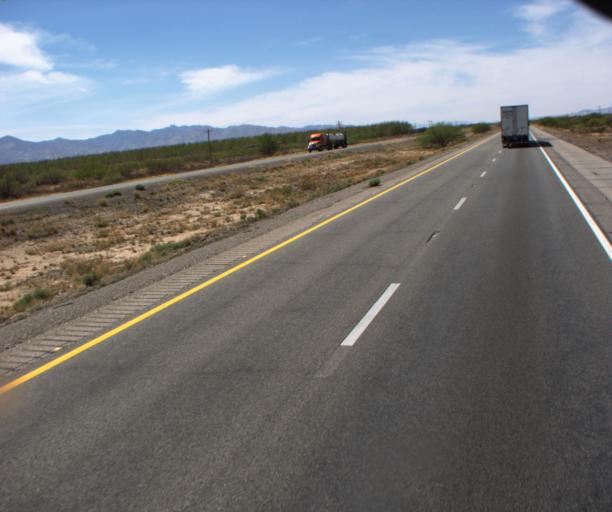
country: US
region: Arizona
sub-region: Cochise County
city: Willcox
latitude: 32.2929
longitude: -109.3340
